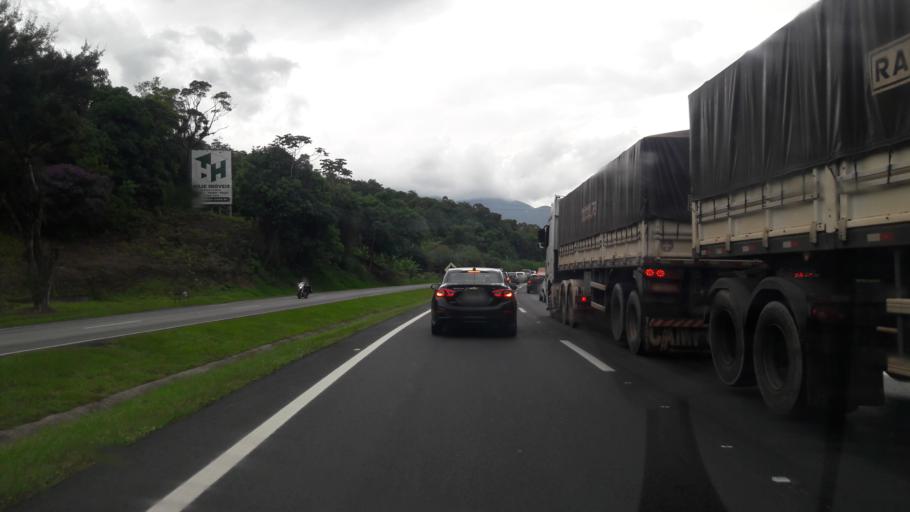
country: BR
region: Parana
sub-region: Antonina
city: Antonina
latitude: -25.5436
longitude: -48.7794
